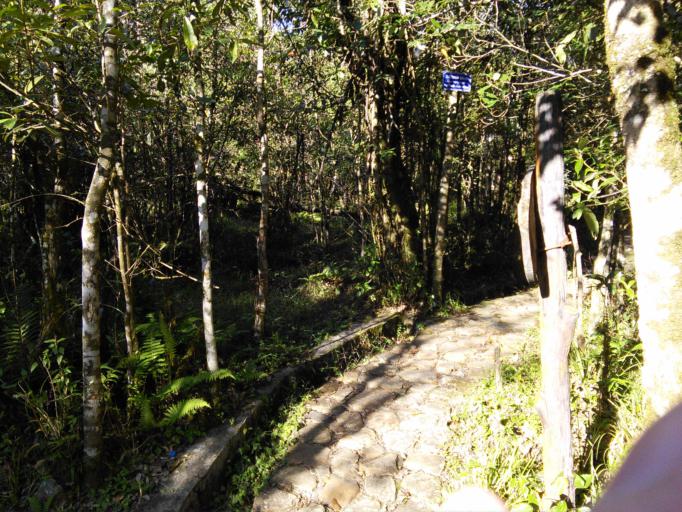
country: VN
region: Lao Cai
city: Sa Pa
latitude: 22.3484
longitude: 103.7704
